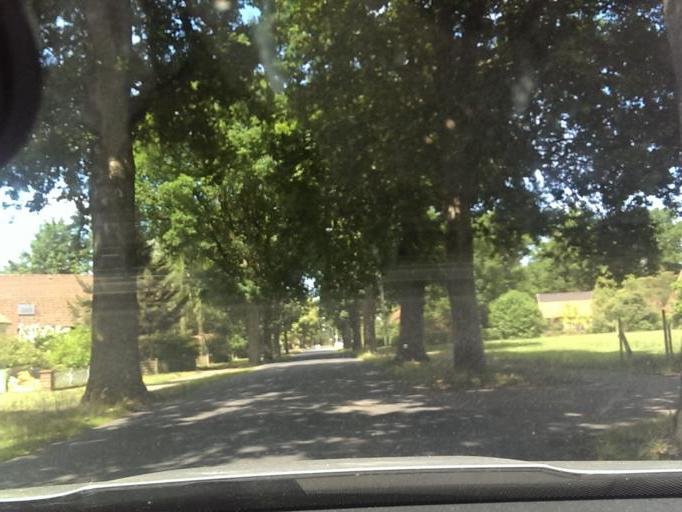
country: DE
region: Lower Saxony
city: Hellwege
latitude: 53.0729
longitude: 9.2413
